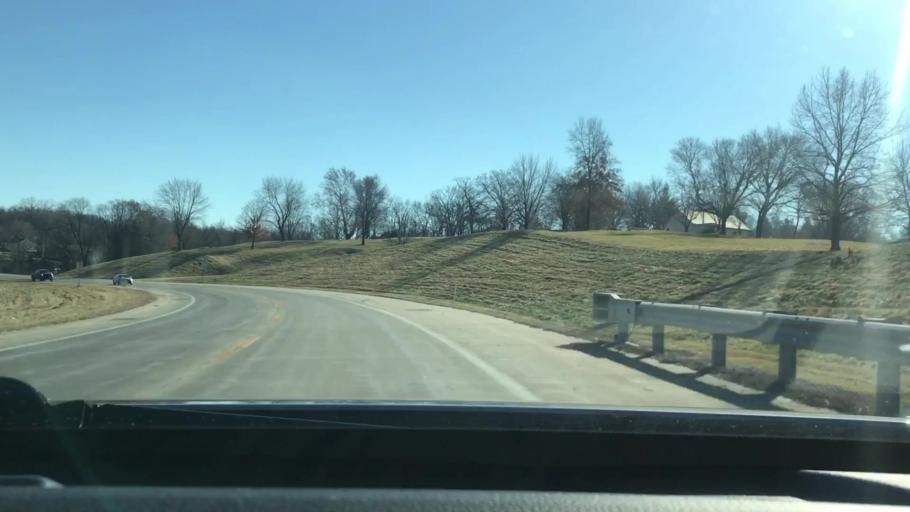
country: US
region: Missouri
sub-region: Platte County
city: Platte City
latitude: 39.3682
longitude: -94.7858
